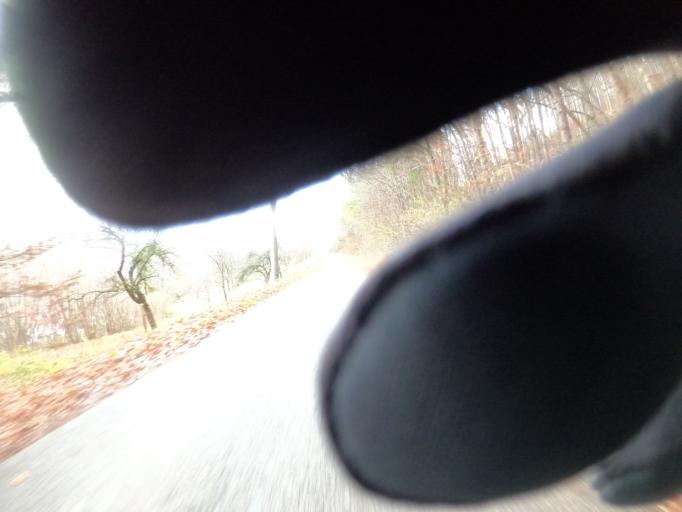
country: DE
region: Baden-Wuerttemberg
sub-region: Regierungsbezirk Stuttgart
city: Waldstetten
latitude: 48.7341
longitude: 9.8420
